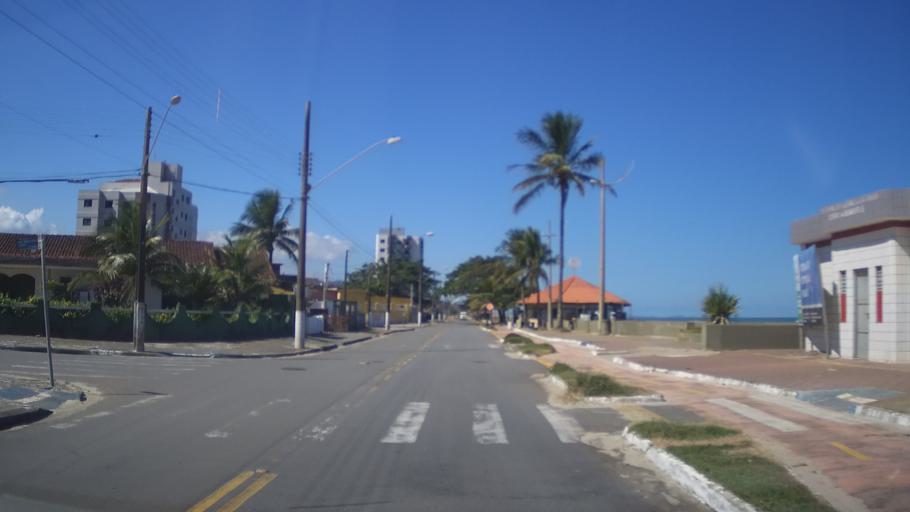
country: BR
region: Sao Paulo
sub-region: Mongagua
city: Mongagua
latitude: -24.1300
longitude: -46.6864
